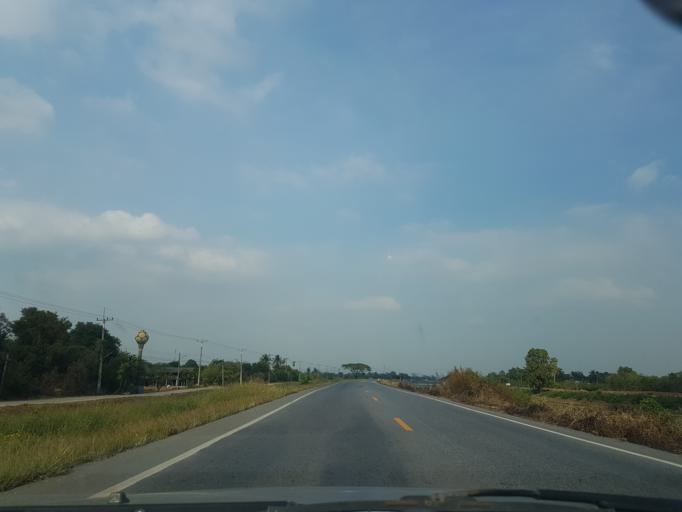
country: TH
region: Phra Nakhon Si Ayutthaya
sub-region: Amphoe Tha Ruea
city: Tha Ruea
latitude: 14.5212
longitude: 100.7386
